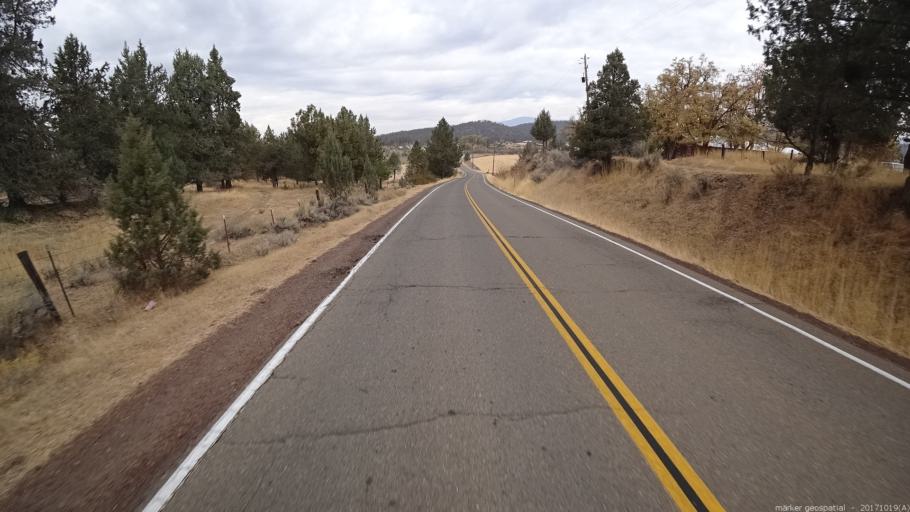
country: US
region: California
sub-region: Shasta County
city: Burney
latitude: 41.0394
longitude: -121.3316
